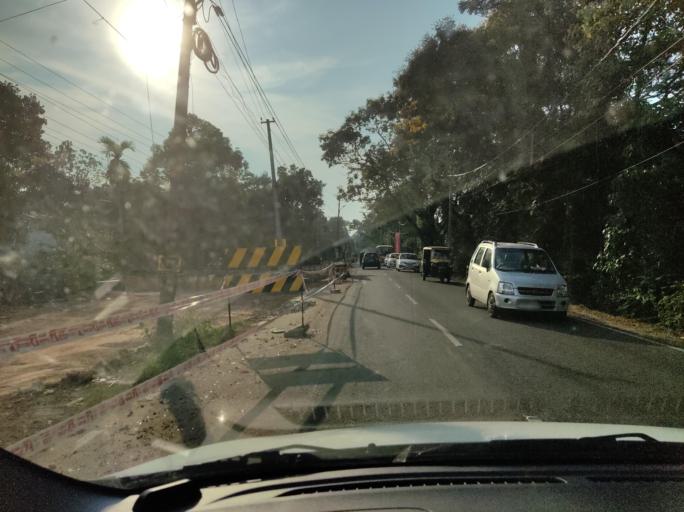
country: IN
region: Kerala
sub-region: Kottayam
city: Kottayam
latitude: 9.6292
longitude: 76.5346
